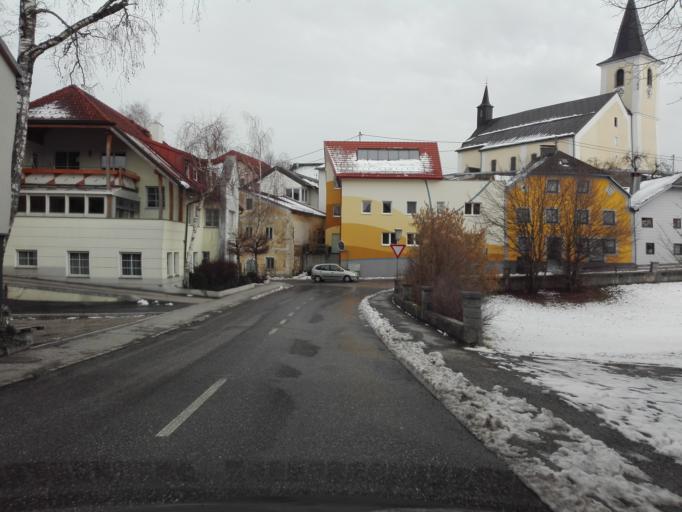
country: AT
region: Upper Austria
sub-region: Politischer Bezirk Rohrbach
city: Atzesberg
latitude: 48.5470
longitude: 13.9033
